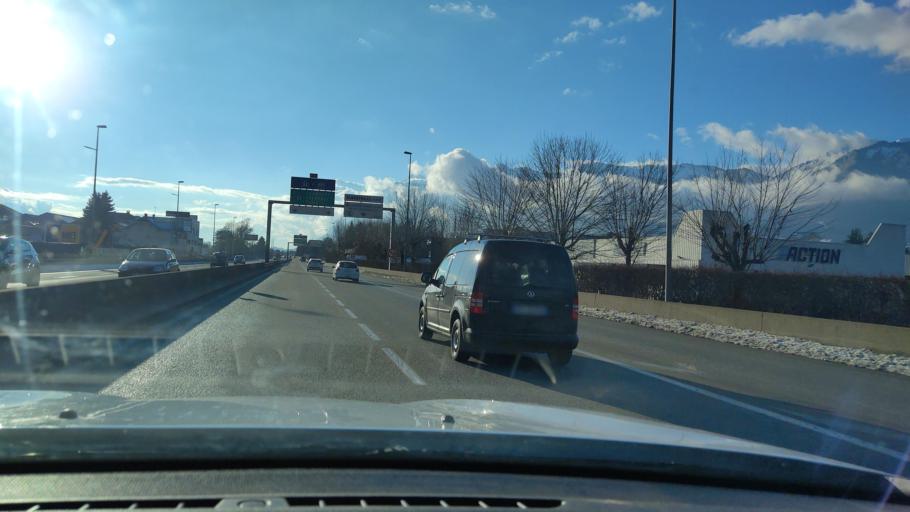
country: FR
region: Rhone-Alpes
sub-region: Departement de la Savoie
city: Grignon
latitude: 45.6614
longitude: 6.3819
